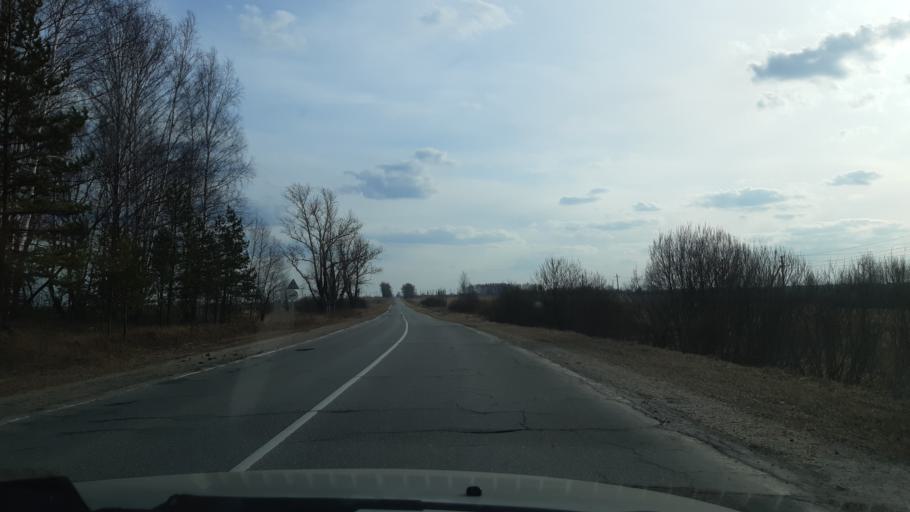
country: RU
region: Vladimir
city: Nikologory
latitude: 56.1732
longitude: 42.0017
